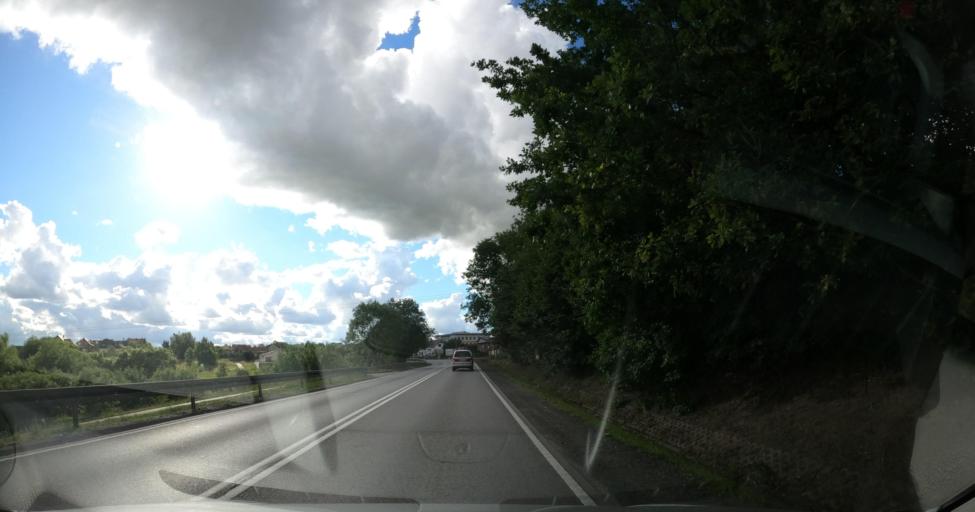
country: PL
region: Pomeranian Voivodeship
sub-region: Powiat kartuski
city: Zukowo
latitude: 54.3401
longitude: 18.3776
